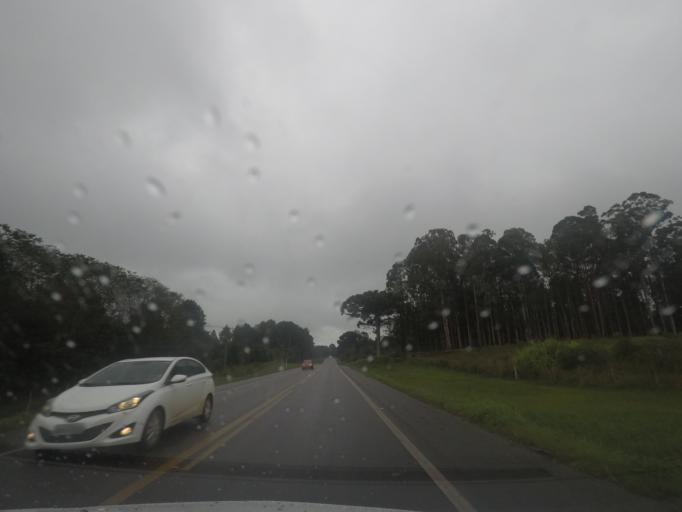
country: BR
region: Parana
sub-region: Colombo
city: Colombo
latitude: -25.3322
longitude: -49.1589
